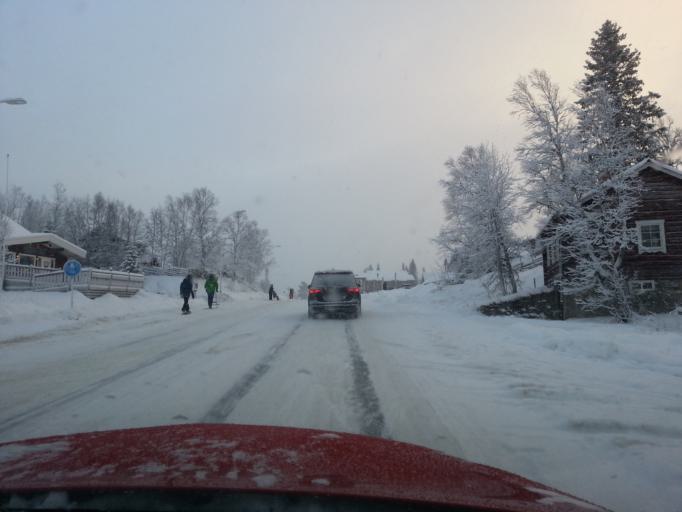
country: SE
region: Jaemtland
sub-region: Bergs Kommun
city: Hoverberg
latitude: 62.4839
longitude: 13.9713
